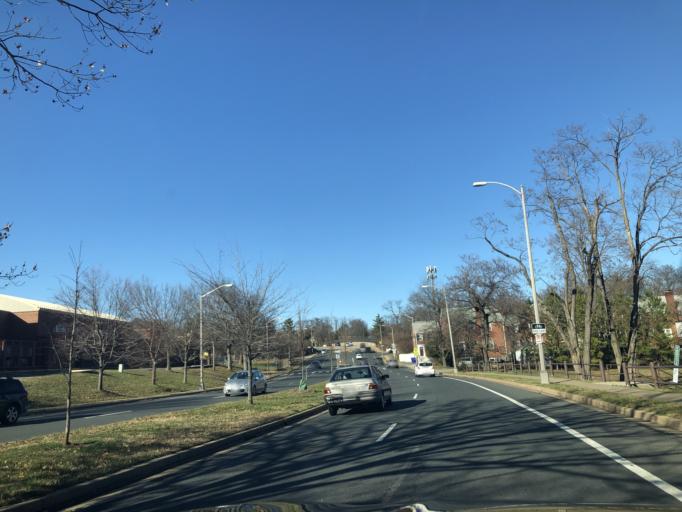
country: US
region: Virginia
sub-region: Arlington County
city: Arlington
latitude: 38.8796
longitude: -77.1210
